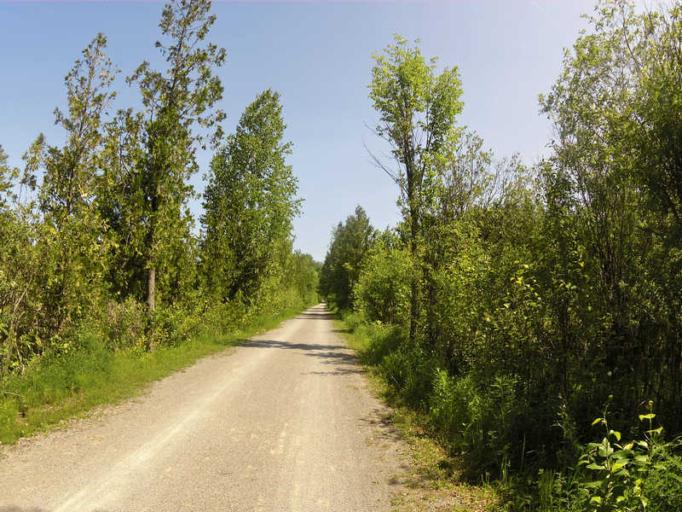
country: CA
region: Ontario
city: Peterborough
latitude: 44.3886
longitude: -78.2676
